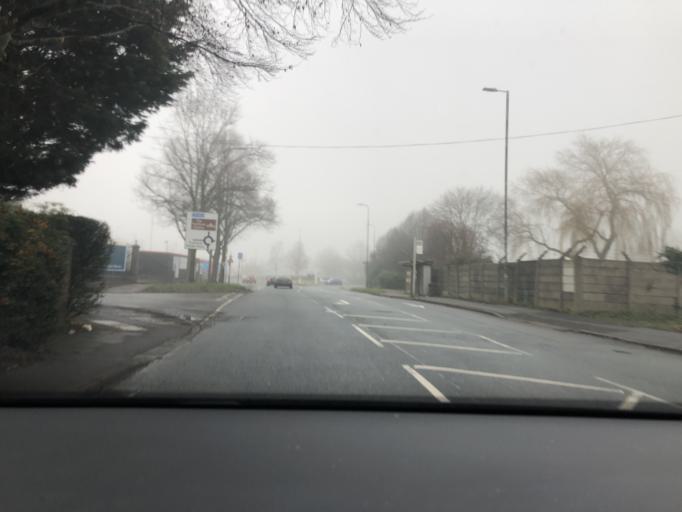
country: GB
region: England
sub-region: Trafford
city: Urmston
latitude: 53.4610
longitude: -2.3581
